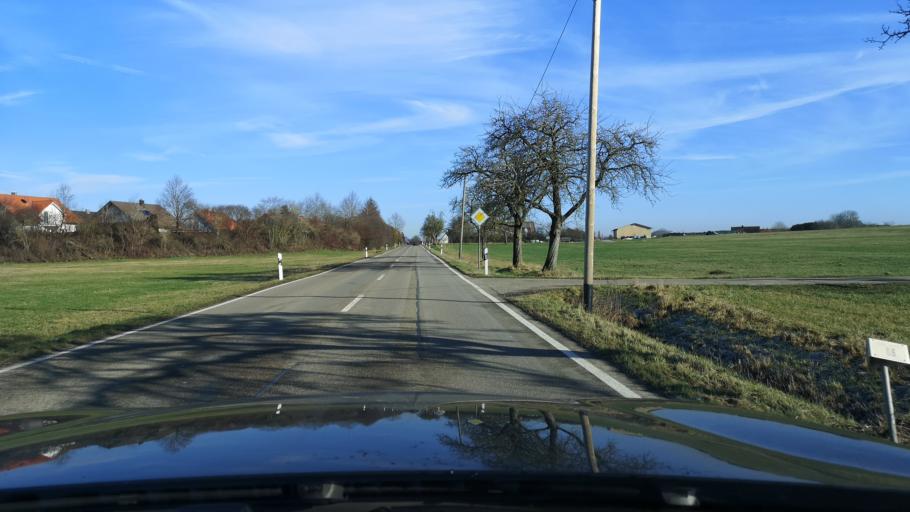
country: DE
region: Baden-Wuerttemberg
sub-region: Regierungsbezirk Stuttgart
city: Obergroningen
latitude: 48.8931
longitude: 9.9021
